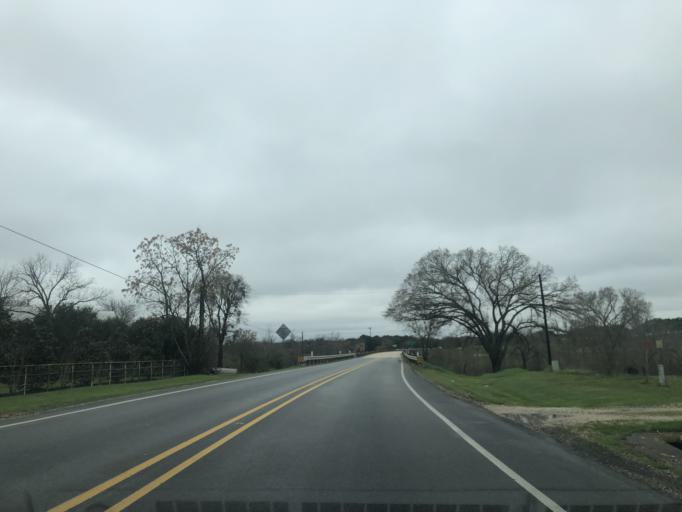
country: US
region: Texas
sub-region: Williamson County
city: Hutto
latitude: 30.6373
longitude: -97.5425
